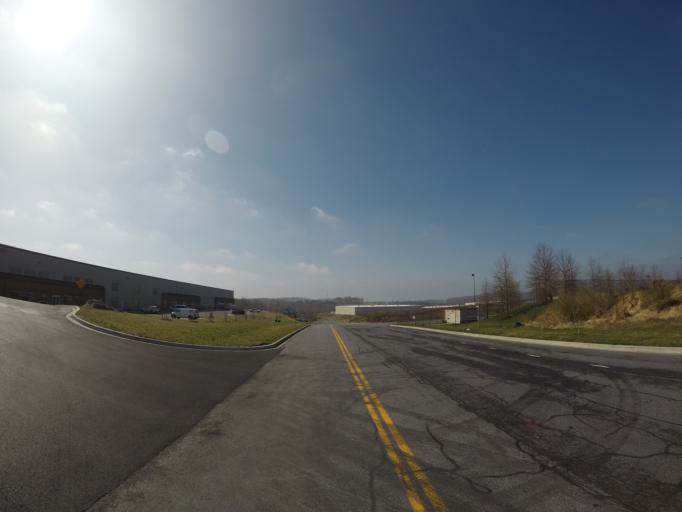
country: US
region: Maryland
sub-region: Frederick County
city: Green Valley
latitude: 39.3777
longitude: -77.2762
